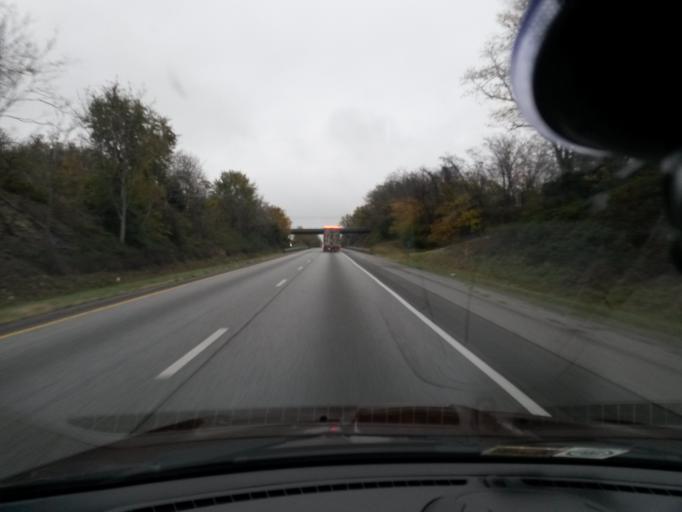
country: US
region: Virginia
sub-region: Botetourt County
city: Daleville
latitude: 37.4186
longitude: -79.8836
